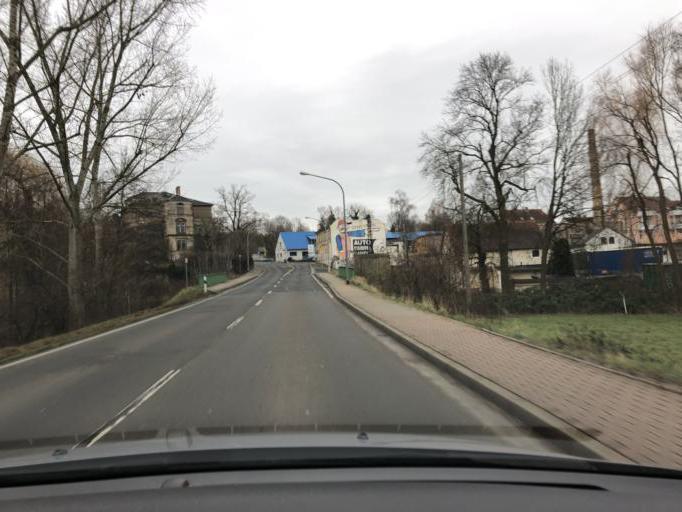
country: DE
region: Saxony
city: Dobeln
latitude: 51.1361
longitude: 13.0994
